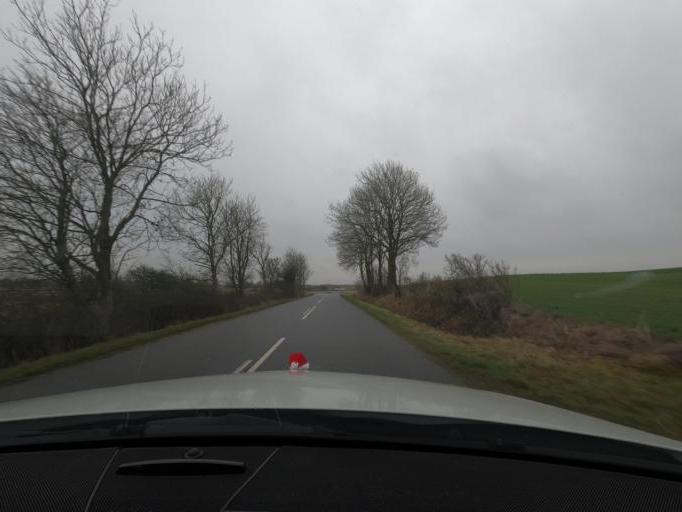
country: DK
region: South Denmark
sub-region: Haderslev Kommune
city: Haderslev
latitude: 55.1950
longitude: 9.4678
